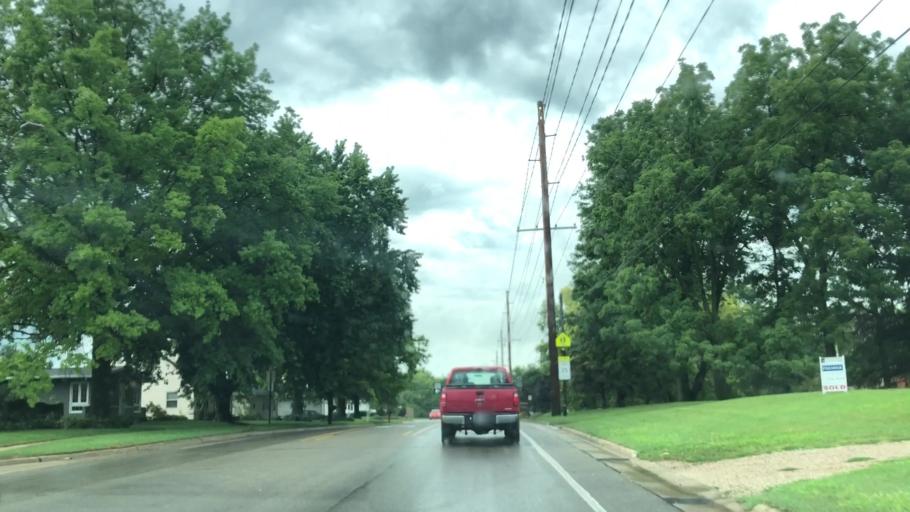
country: US
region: Iowa
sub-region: Marshall County
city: Marshalltown
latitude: 42.0265
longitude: -92.9222
